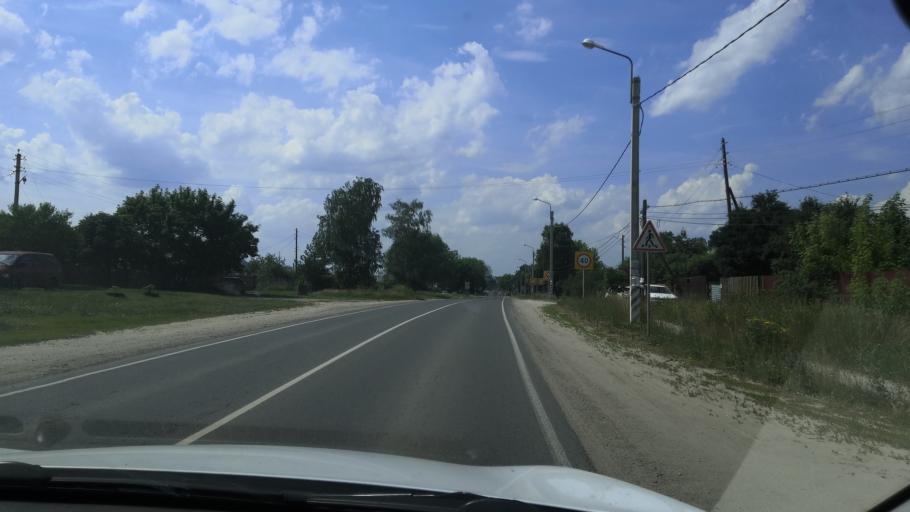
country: RU
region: Rjazan
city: Murmino
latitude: 54.6038
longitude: 40.0466
